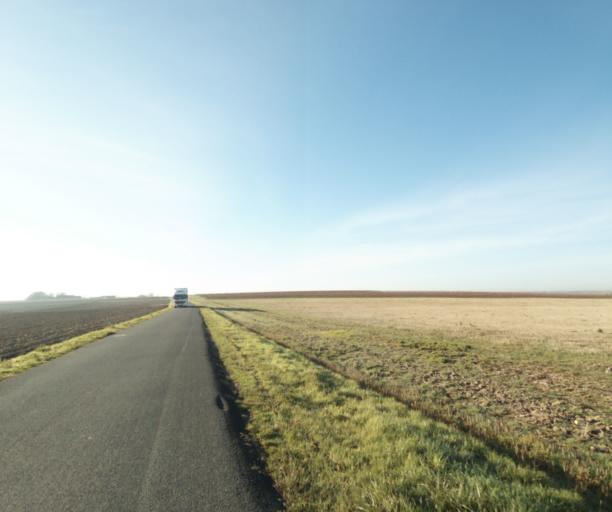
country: FR
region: Poitou-Charentes
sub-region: Departement de la Charente-Maritime
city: Cherac
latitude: 45.6951
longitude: -0.4488
